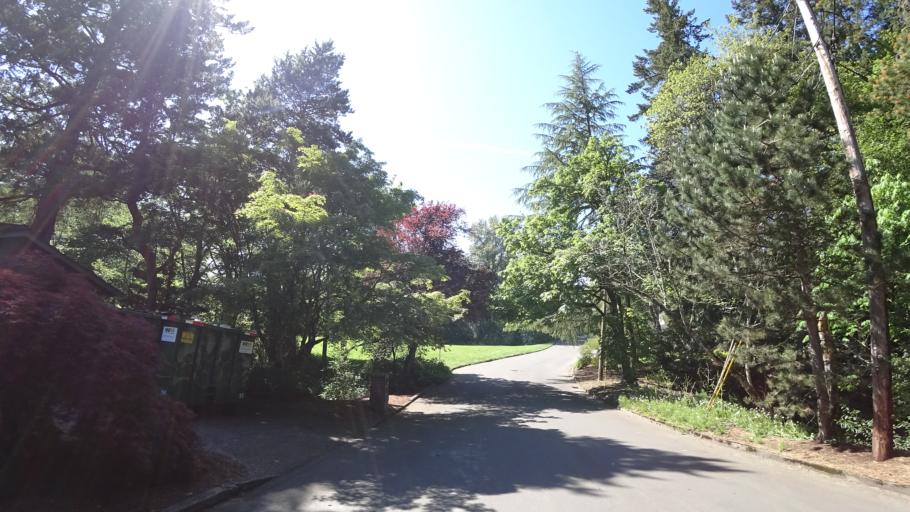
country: US
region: Oregon
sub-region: Washington County
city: West Slope
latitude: 45.4945
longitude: -122.7317
